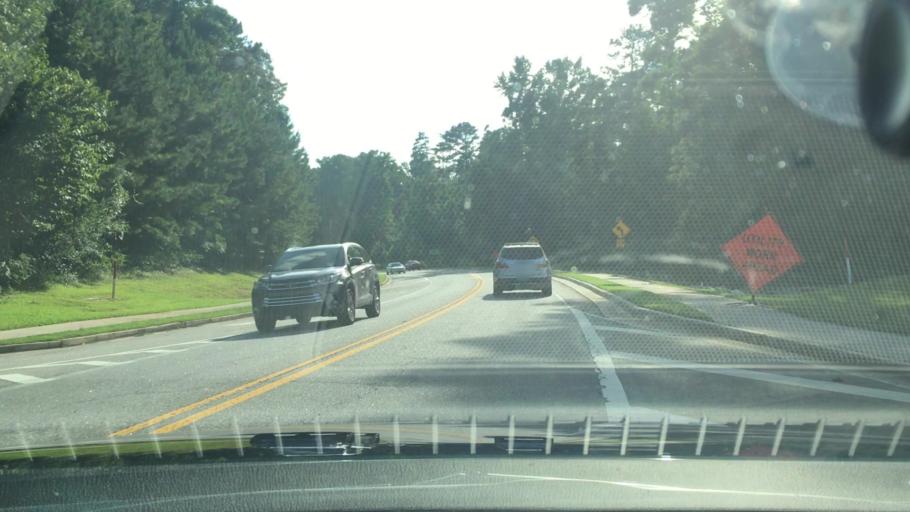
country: US
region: Georgia
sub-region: Coweta County
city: East Newnan
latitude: 33.3807
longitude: -84.7426
